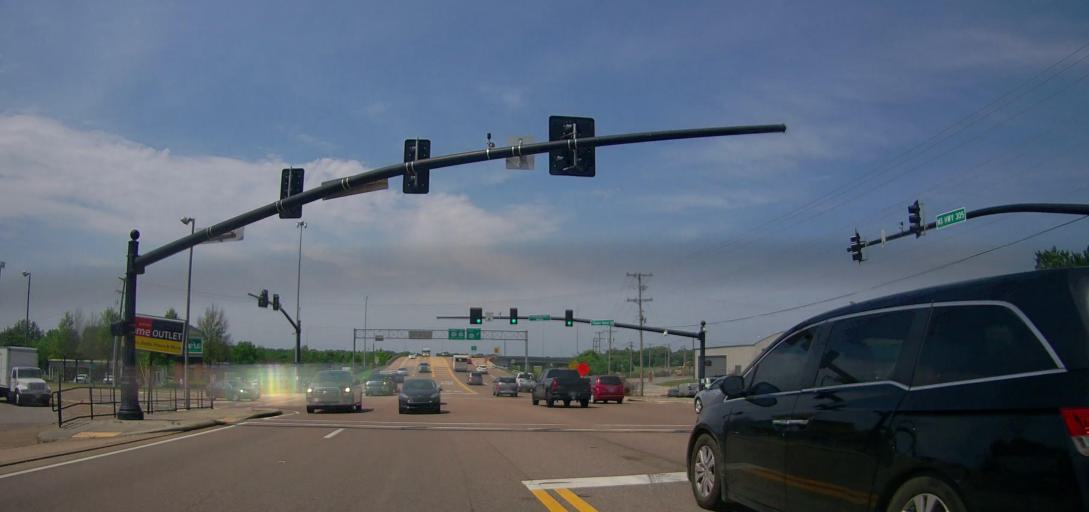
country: US
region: Mississippi
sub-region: De Soto County
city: Olive Branch
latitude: 34.9638
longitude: -89.8304
